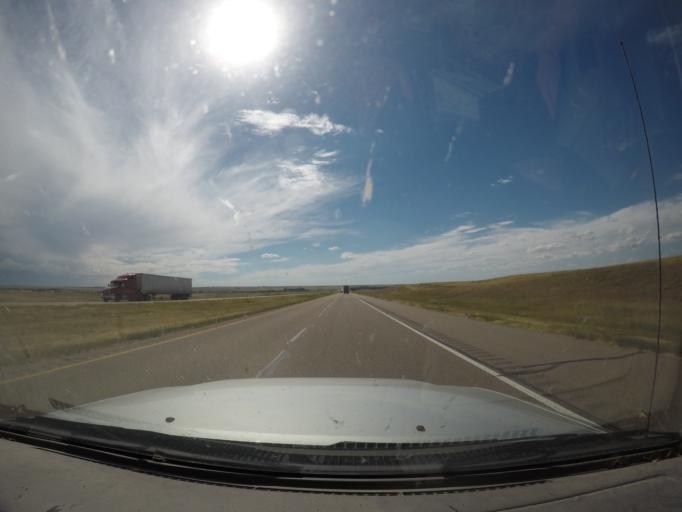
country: US
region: Nebraska
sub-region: Deuel County
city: Chappell
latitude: 41.0520
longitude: -102.3909
